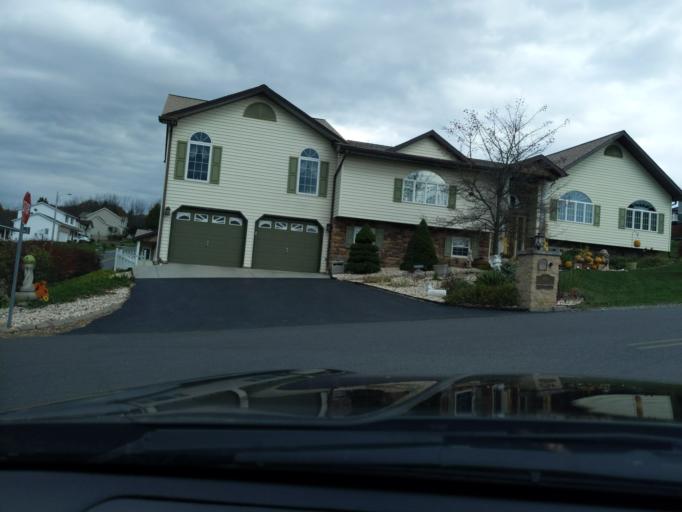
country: US
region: Pennsylvania
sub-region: Blair County
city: Greenwood
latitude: 40.5350
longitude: -78.3661
